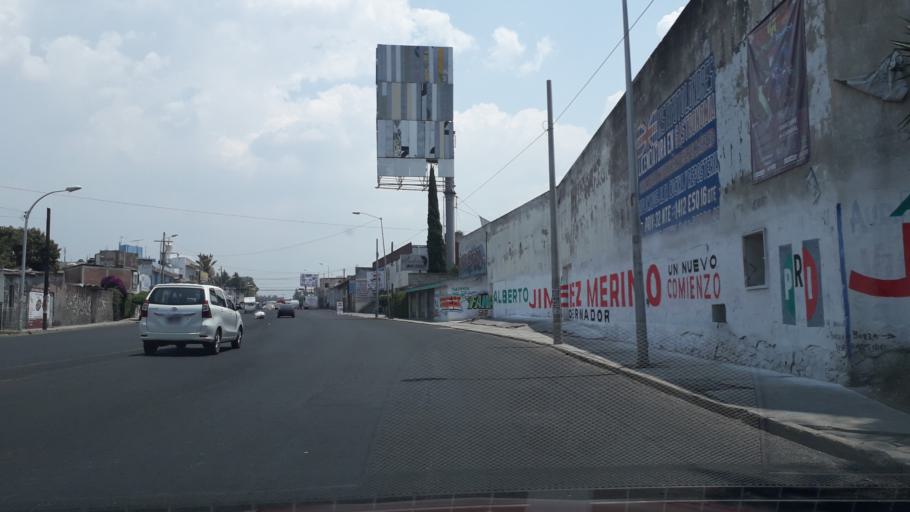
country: MX
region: Puebla
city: Puebla
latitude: 19.0459
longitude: -98.1767
